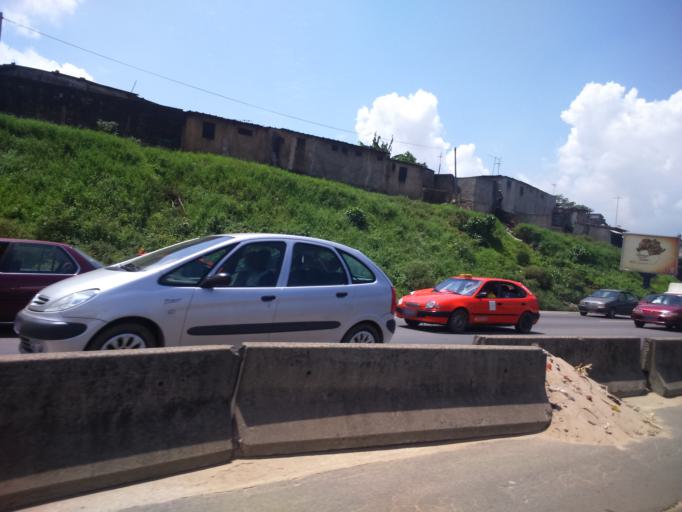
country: CI
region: Lagunes
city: Abobo
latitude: 5.3628
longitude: -4.0244
